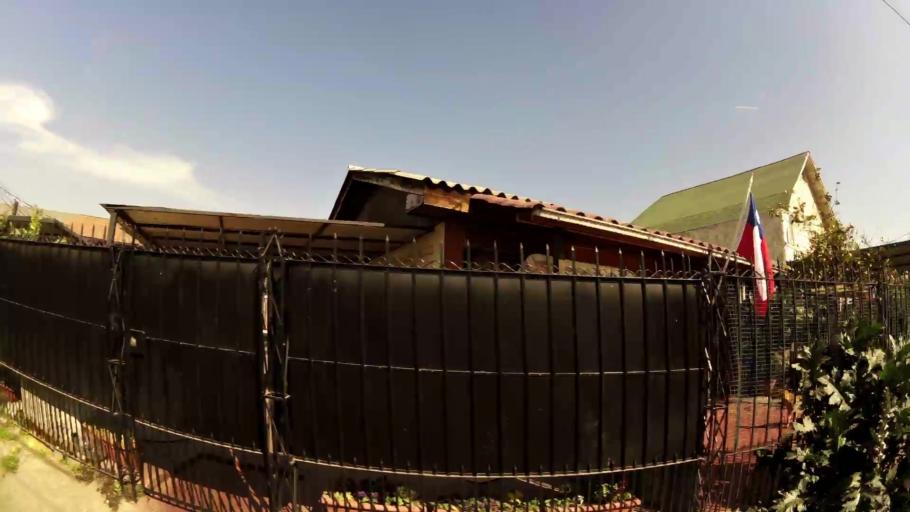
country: CL
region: Santiago Metropolitan
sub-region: Provincia de Santiago
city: La Pintana
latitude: -33.5484
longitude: -70.5901
